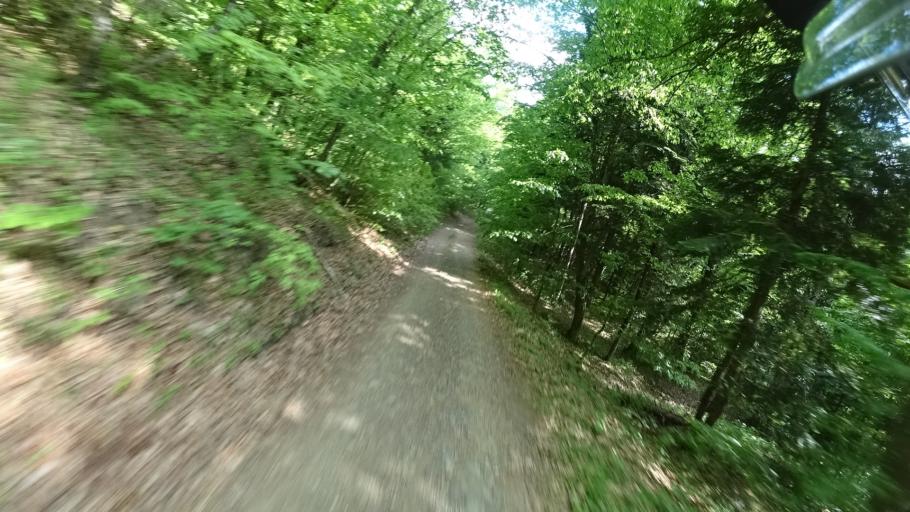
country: HR
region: Grad Zagreb
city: Kasina
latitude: 45.9340
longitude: 15.9405
